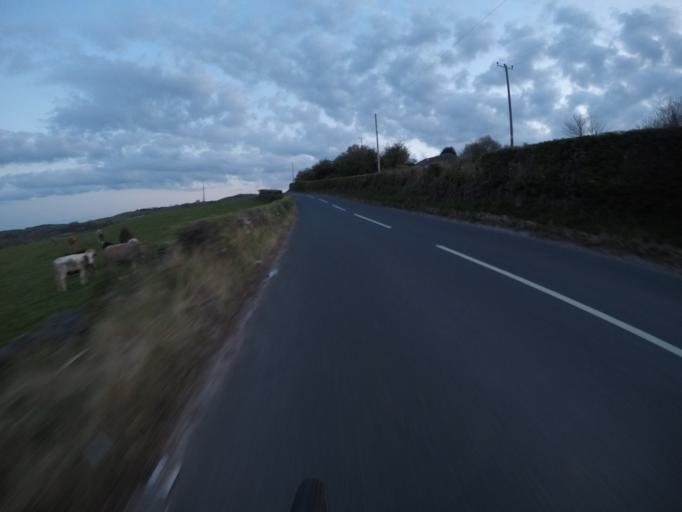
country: GB
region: Scotland
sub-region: South Ayrshire
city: Dundonald
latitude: 55.5670
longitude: -4.6010
